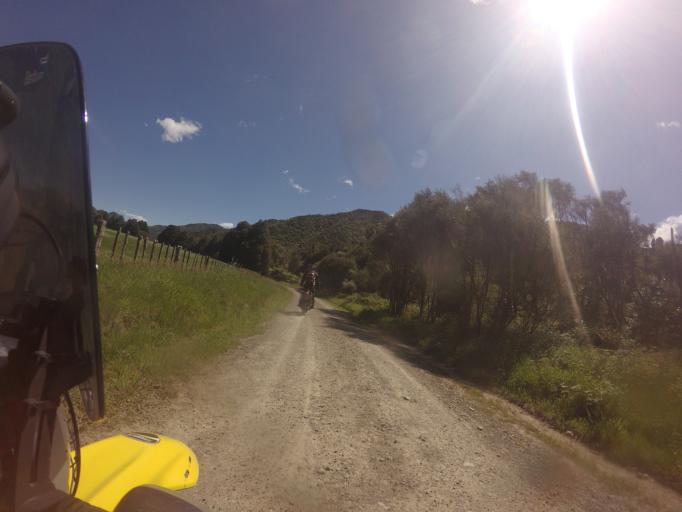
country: NZ
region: Bay of Plenty
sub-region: Opotiki District
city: Opotiki
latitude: -38.2973
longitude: 177.3362
